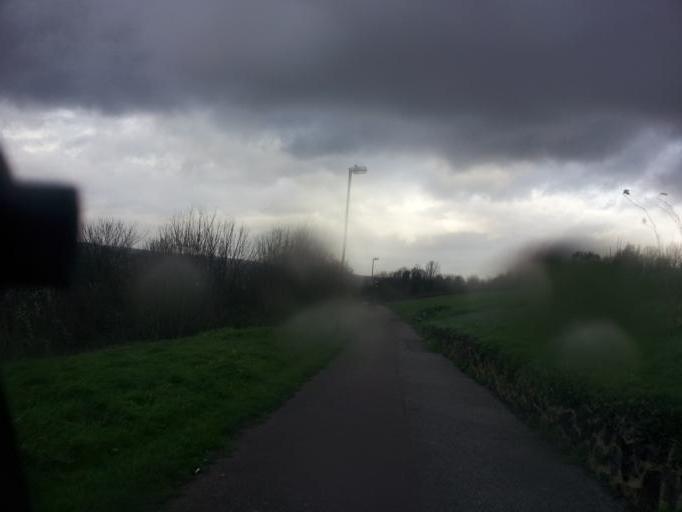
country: GB
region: England
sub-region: Kent
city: Chatham
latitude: 51.3821
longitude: 0.5325
